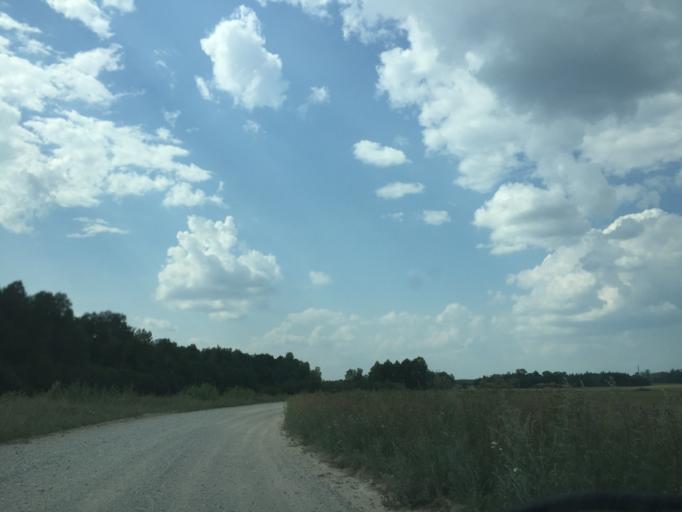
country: LV
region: Auces Novads
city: Auce
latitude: 56.4029
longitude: 23.0519
